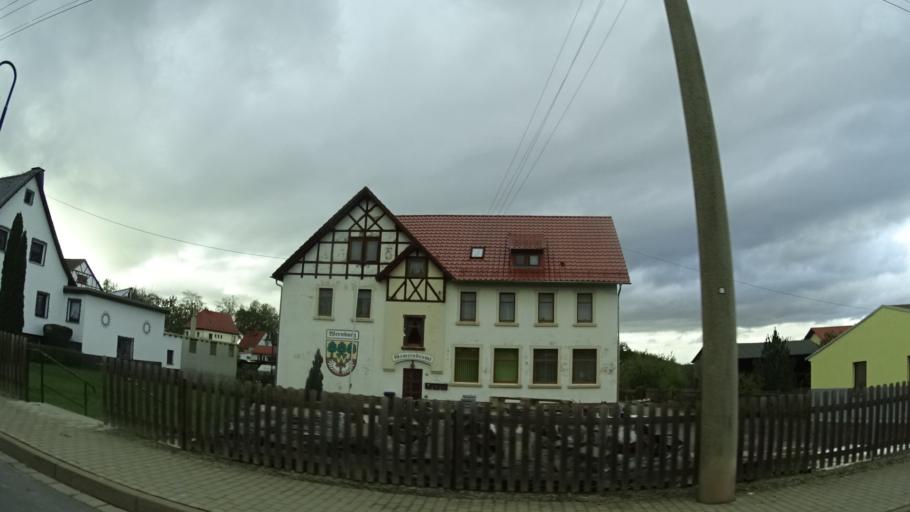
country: DE
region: Thuringia
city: Wernburg
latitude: 50.6799
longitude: 11.6030
